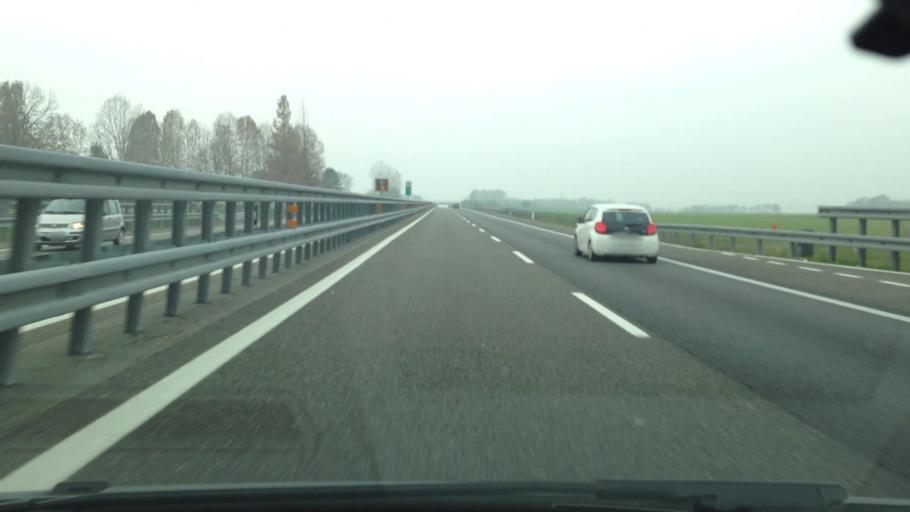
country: IT
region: Piedmont
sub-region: Provincia di Torino
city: Marocchi
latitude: 44.9587
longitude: 7.8125
